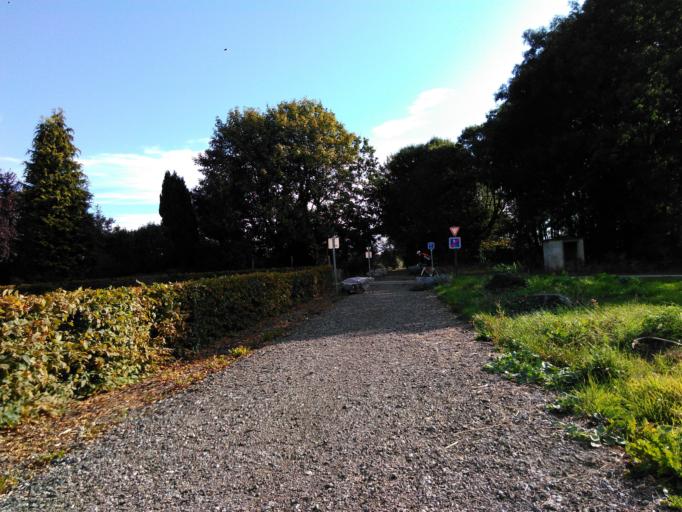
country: BE
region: Wallonia
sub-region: Province du Luxembourg
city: Neufchateau
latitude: 49.9171
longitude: 5.4007
